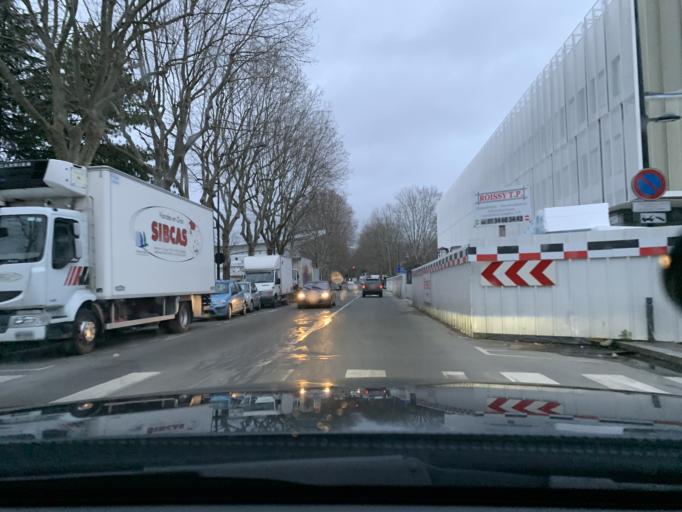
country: FR
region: Ile-de-France
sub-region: Departement de Seine-Saint-Denis
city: Saint-Denis
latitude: 48.9404
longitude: 2.3634
